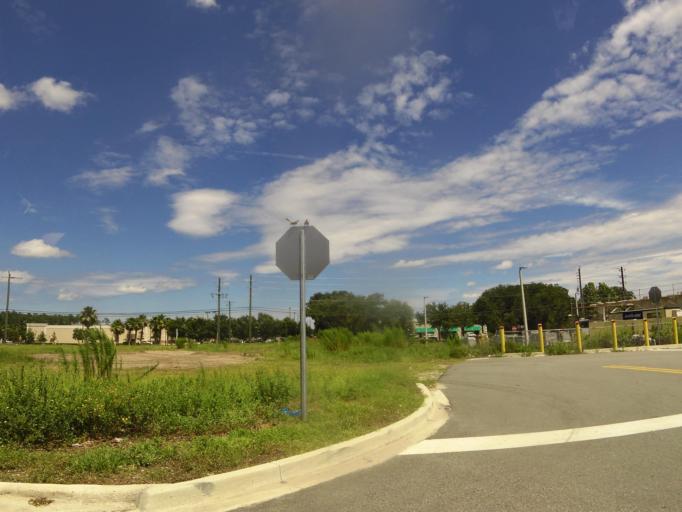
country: US
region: Florida
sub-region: Nassau County
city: Yulee
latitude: 30.6277
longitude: -81.5480
